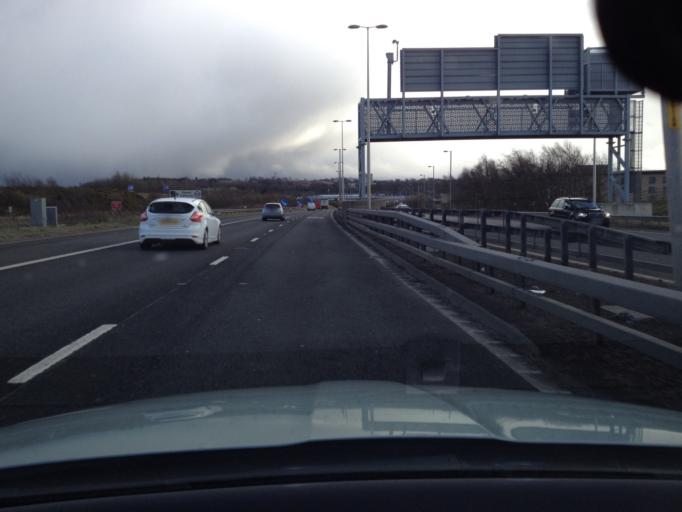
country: GB
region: Scotland
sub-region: Edinburgh
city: Kirkliston
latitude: 55.9444
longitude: -3.4055
